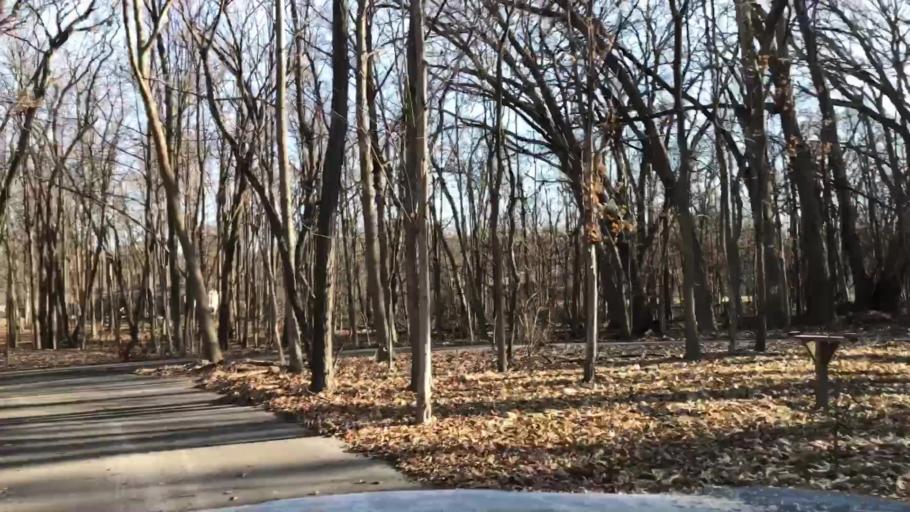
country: US
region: Illinois
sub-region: McLean County
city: Hudson
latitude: 40.6472
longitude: -88.9151
